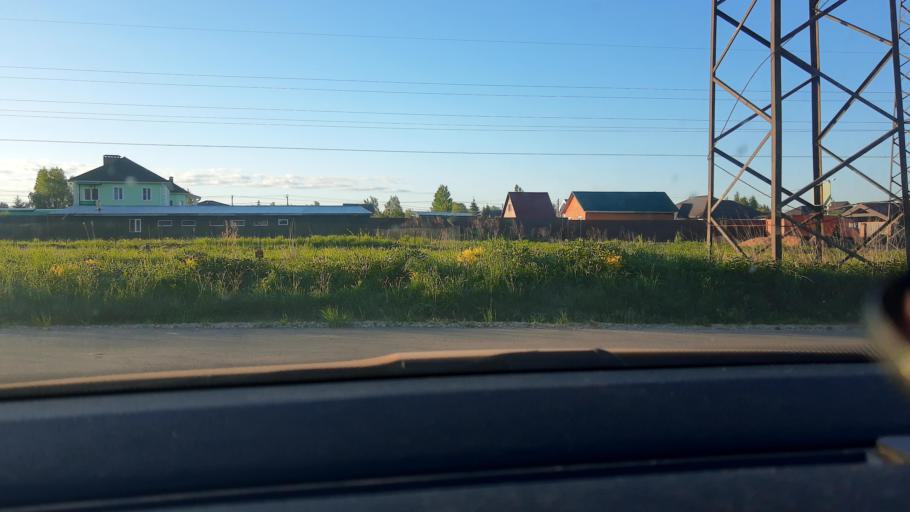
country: RU
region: Moskovskaya
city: Selyatino
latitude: 55.5064
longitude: 36.9248
